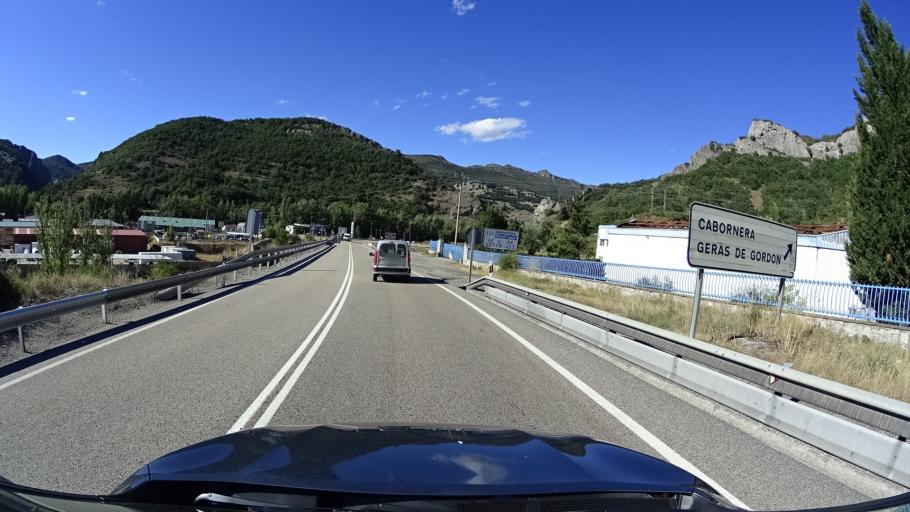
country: ES
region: Castille and Leon
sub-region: Provincia de Leon
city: La Pola de Gordon
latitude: 42.8602
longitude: -5.6736
